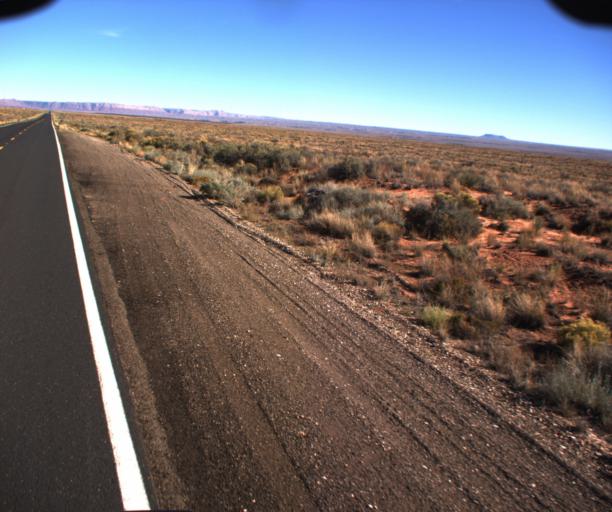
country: US
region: Arizona
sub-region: Coconino County
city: Page
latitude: 36.7036
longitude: -111.9416
